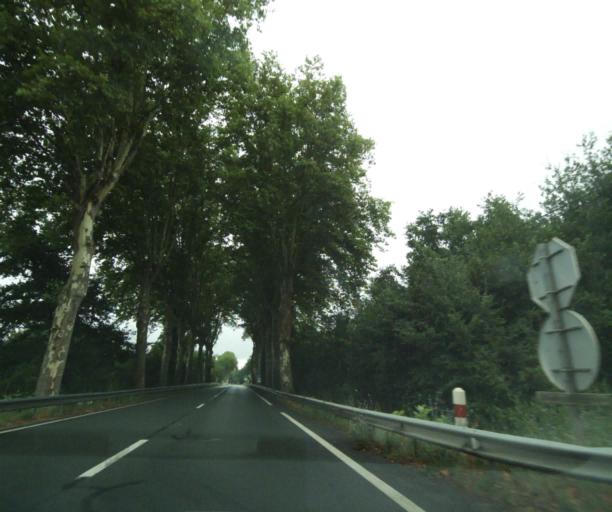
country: FR
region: Midi-Pyrenees
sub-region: Departement du Tarn
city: Le Garric
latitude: 43.9757
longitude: 2.1791
